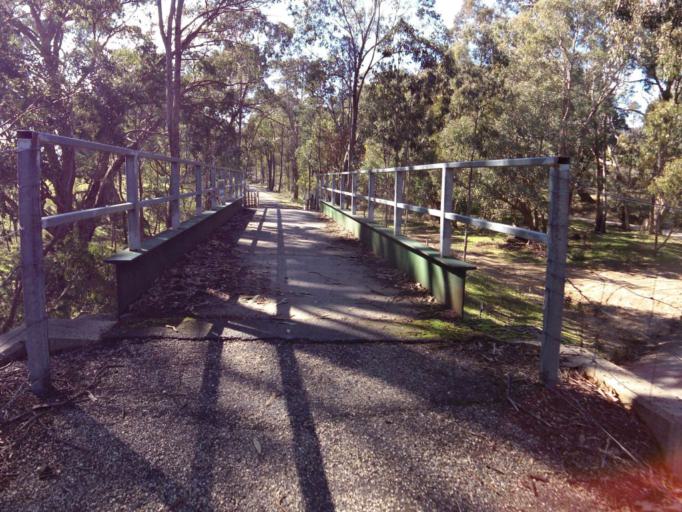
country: AU
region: Victoria
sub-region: Wangaratta
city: Wangaratta
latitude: -36.4032
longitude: 146.6394
